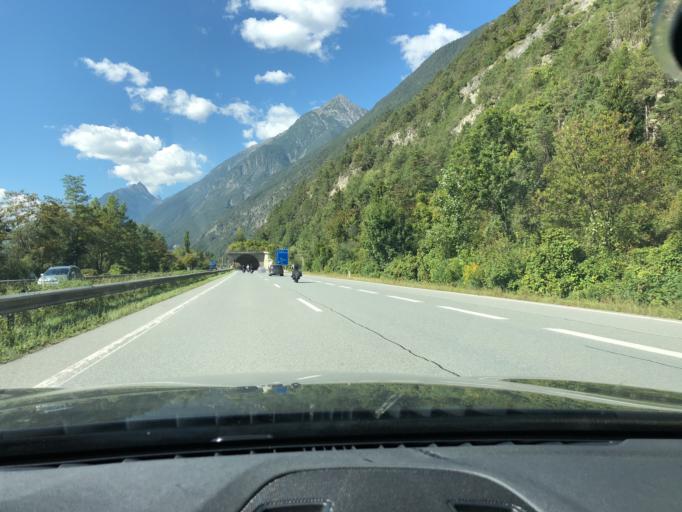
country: AT
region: Tyrol
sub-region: Politischer Bezirk Imst
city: Imsterberg
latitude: 47.2167
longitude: 10.7154
